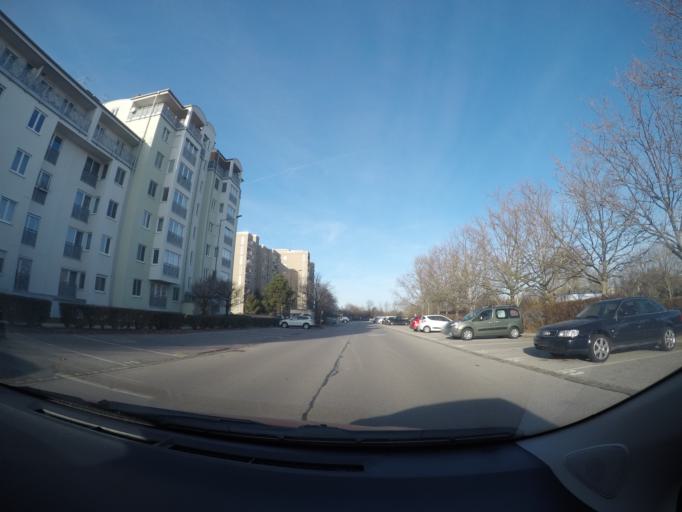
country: AT
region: Lower Austria
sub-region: Politischer Bezirk Modling
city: Wiener Neudorf
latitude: 48.0888
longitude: 16.3123
